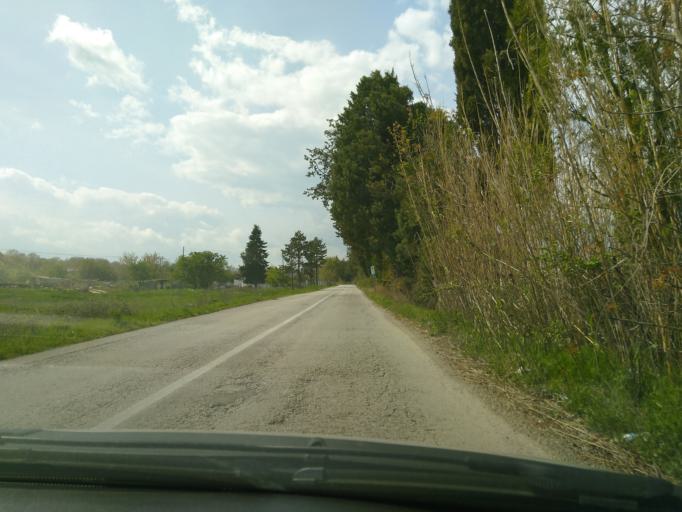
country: GR
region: Epirus
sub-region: Nomos Ioanninon
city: Eleousa
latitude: 39.7357
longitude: 20.7746
